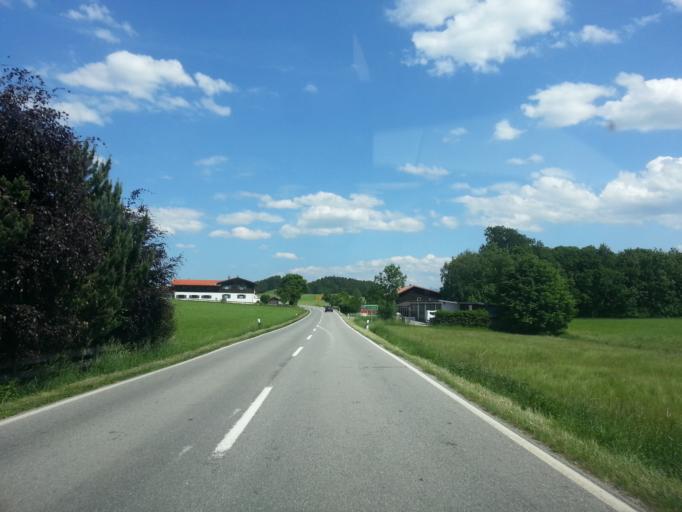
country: DE
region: Bavaria
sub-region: Upper Bavaria
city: Irschenberg
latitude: 47.8055
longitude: 11.9228
